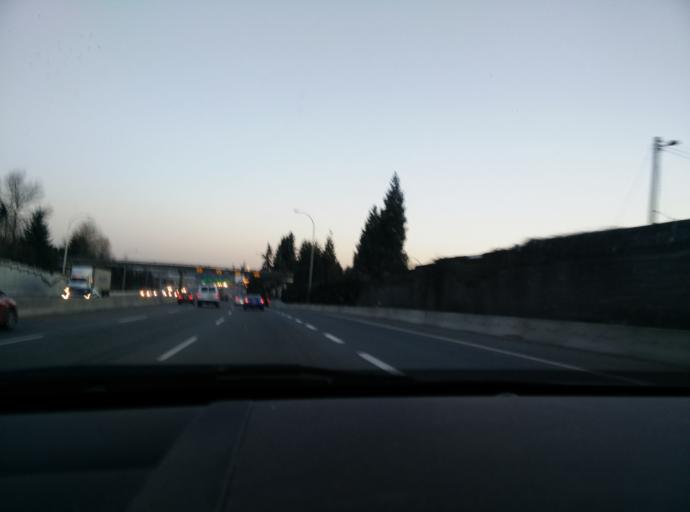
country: CA
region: British Columbia
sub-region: Fraser Valley Regional District
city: North Vancouver
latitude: 49.2749
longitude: -123.0312
